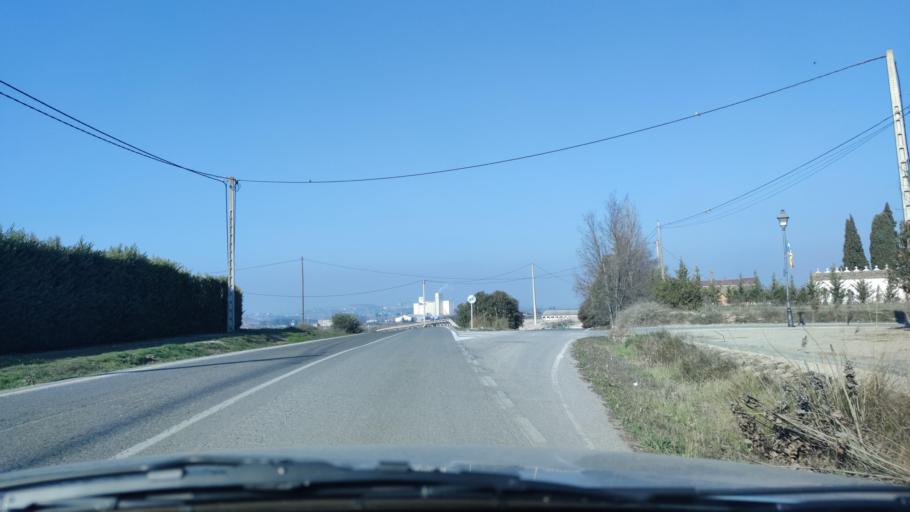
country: ES
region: Catalonia
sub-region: Provincia de Lleida
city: Alcoletge
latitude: 41.6206
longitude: 0.7303
